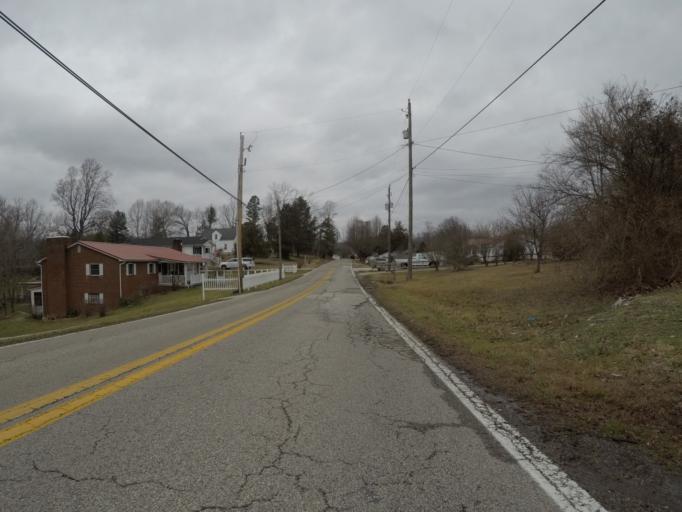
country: US
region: West Virginia
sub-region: Cabell County
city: Barboursville
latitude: 38.4305
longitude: -82.2427
